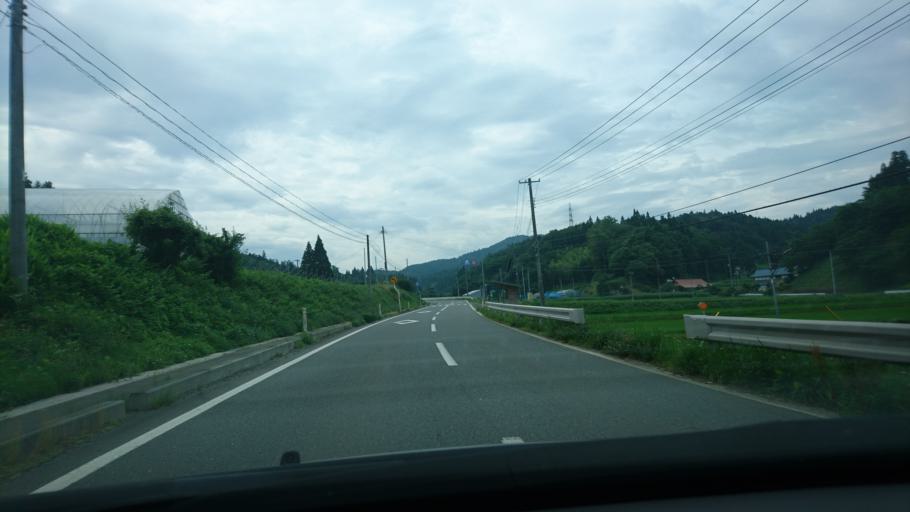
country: JP
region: Iwate
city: Ichinoseki
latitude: 38.8975
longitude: 141.4251
